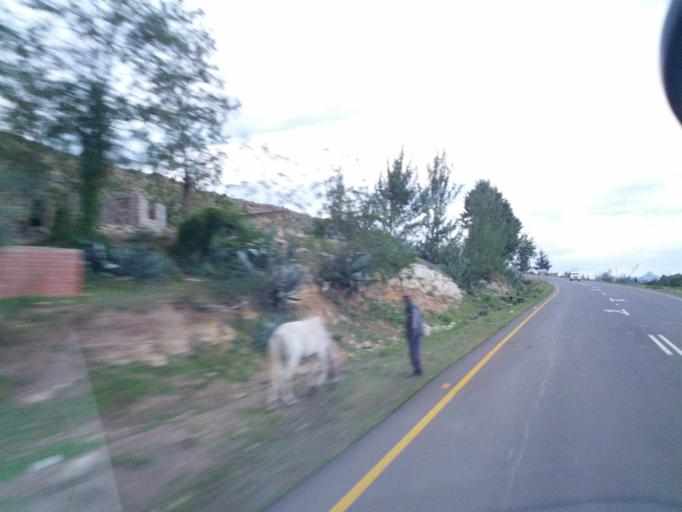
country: LS
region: Qacha's Nek
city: Qacha's Nek
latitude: -30.0305
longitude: 28.3101
